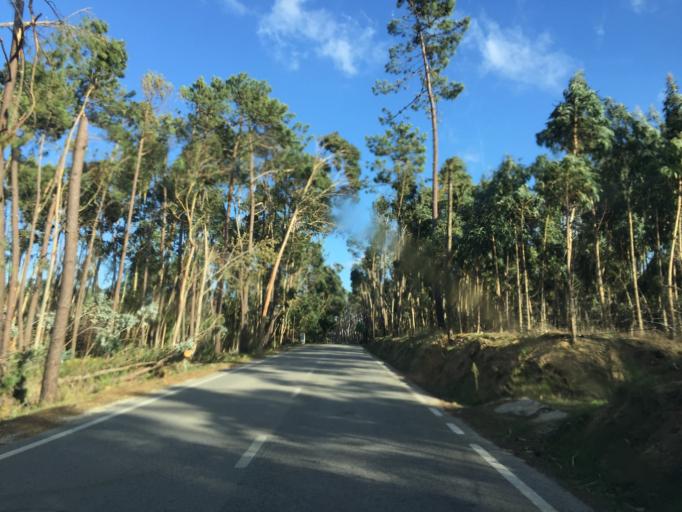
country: PT
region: Coimbra
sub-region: Figueira da Foz
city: Buarcos
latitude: 40.2155
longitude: -8.8697
